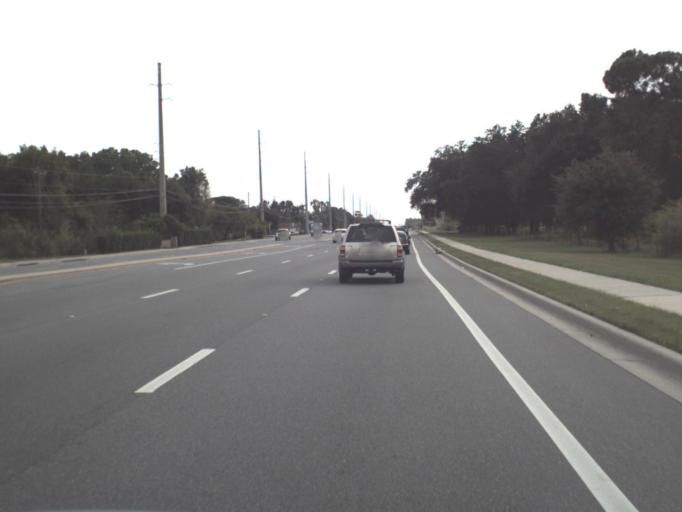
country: US
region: Florida
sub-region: Orange County
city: Meadow Woods
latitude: 28.3930
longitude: -81.2444
